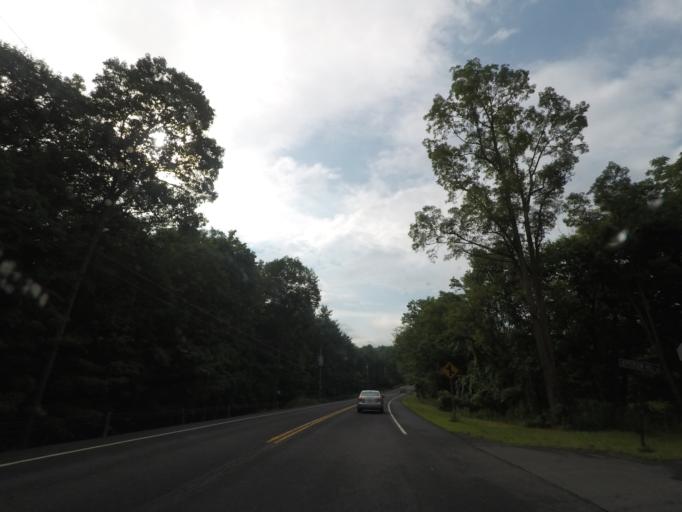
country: US
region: New York
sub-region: Rensselaer County
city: Nassau
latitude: 42.5015
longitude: -73.5580
